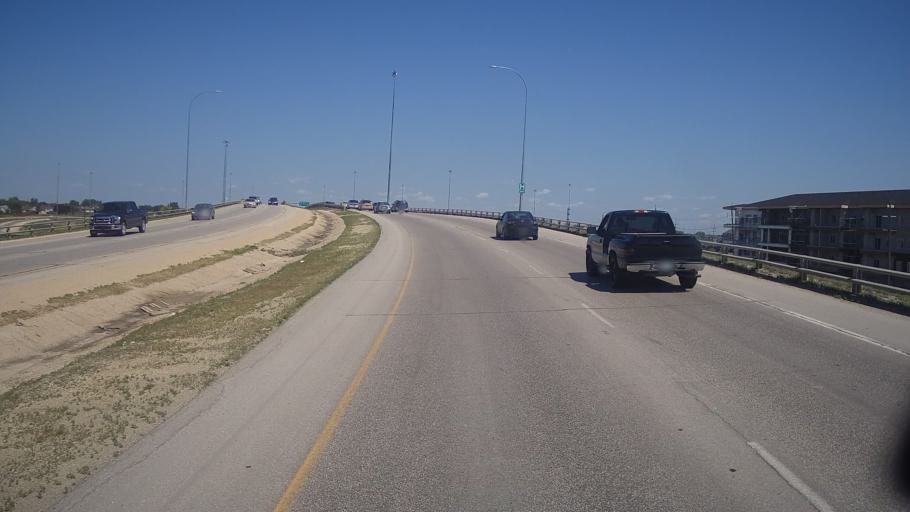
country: CA
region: Manitoba
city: Winnipeg
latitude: 49.9089
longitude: -97.0580
